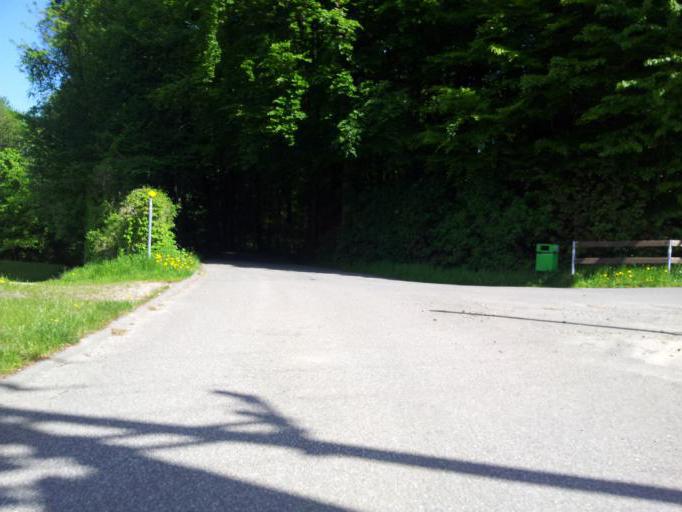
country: CH
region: Aargau
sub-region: Bezirk Bremgarten
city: Rudolfstetten
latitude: 47.3880
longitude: 8.3723
